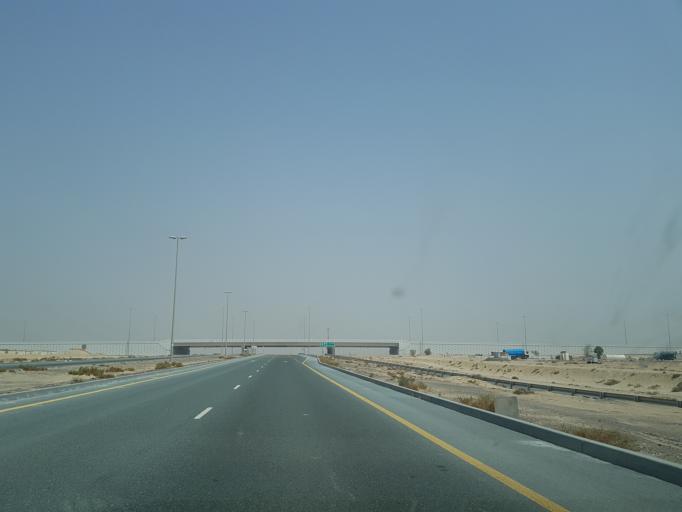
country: AE
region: Dubai
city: Dubai
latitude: 25.0555
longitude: 55.3036
